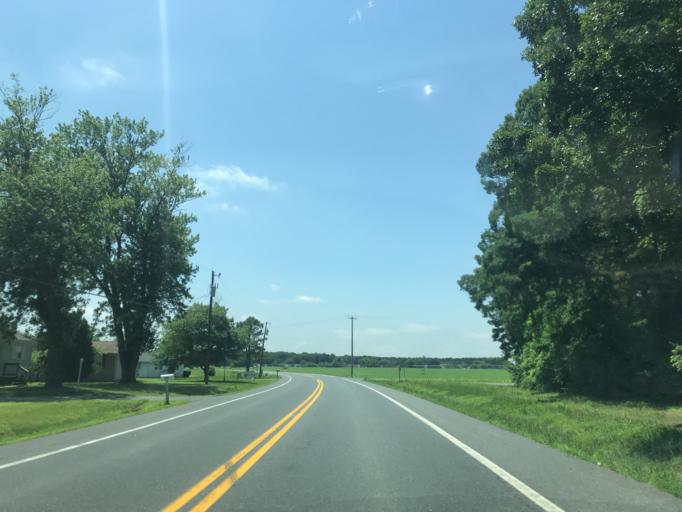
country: US
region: Maryland
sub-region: Dorchester County
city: Hurlock
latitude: 38.6343
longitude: -75.8380
